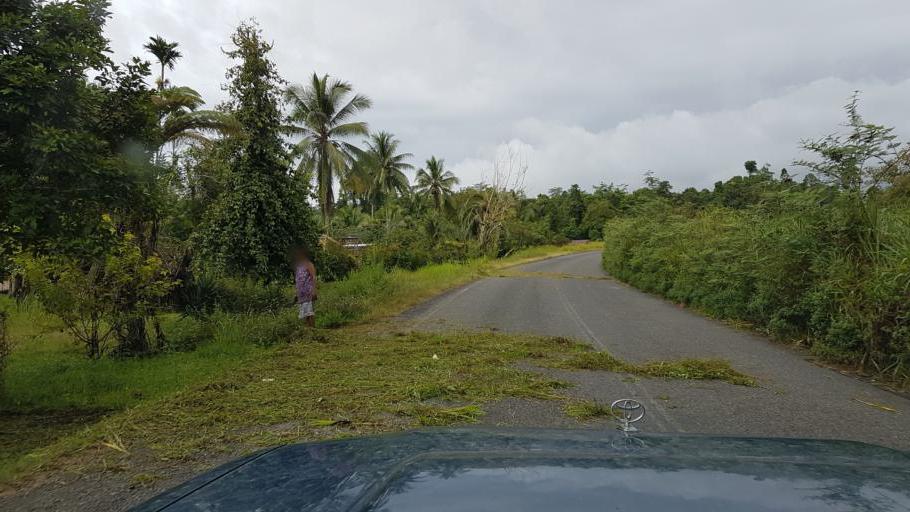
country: PG
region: Northern Province
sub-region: Sohe
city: Popondetta
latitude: -8.8267
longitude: 148.2864
